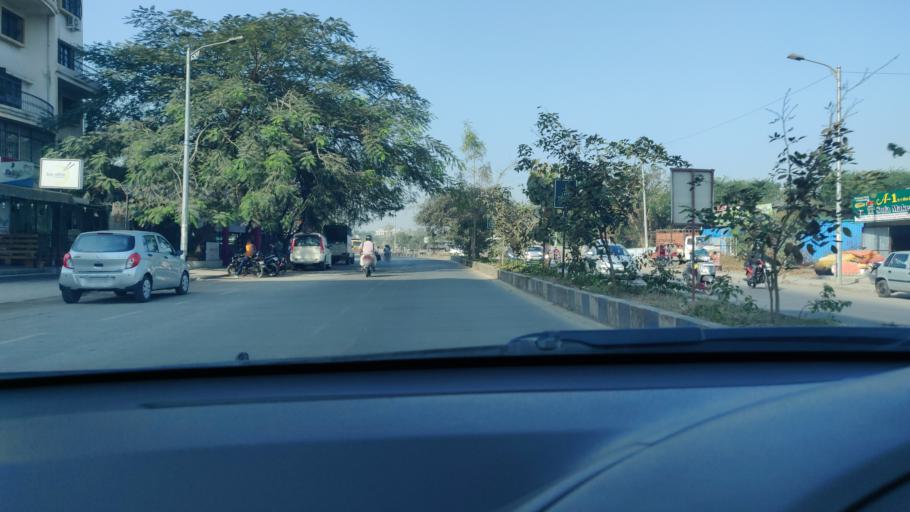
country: IN
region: Maharashtra
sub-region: Pune Division
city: Khadki
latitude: 18.5655
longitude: 73.8008
